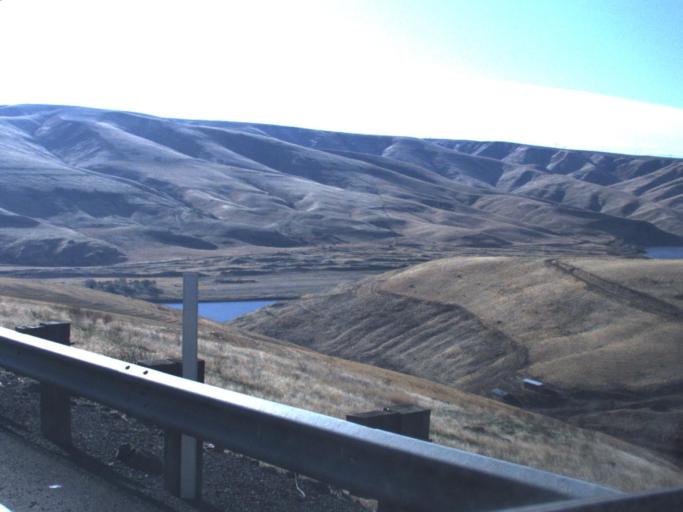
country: US
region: Washington
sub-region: Whitman County
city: Colfax
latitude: 46.7123
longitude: -117.4809
